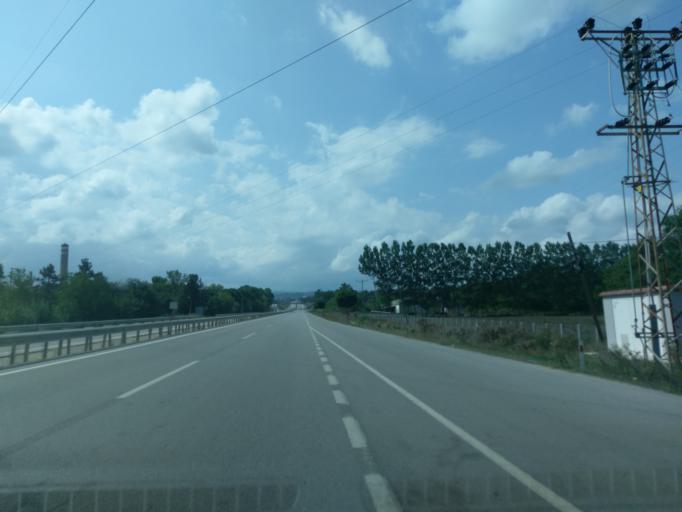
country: TR
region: Sinop
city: Kabali
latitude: 41.9250
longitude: 35.0811
